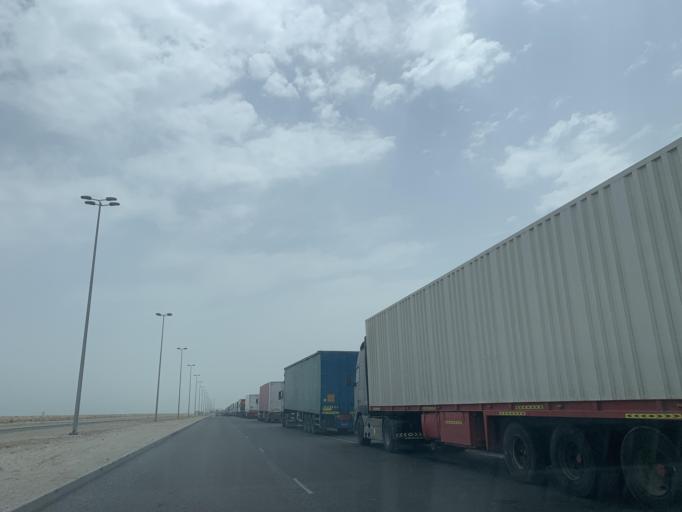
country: BH
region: Muharraq
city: Al Hadd
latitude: 26.2065
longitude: 50.7064
